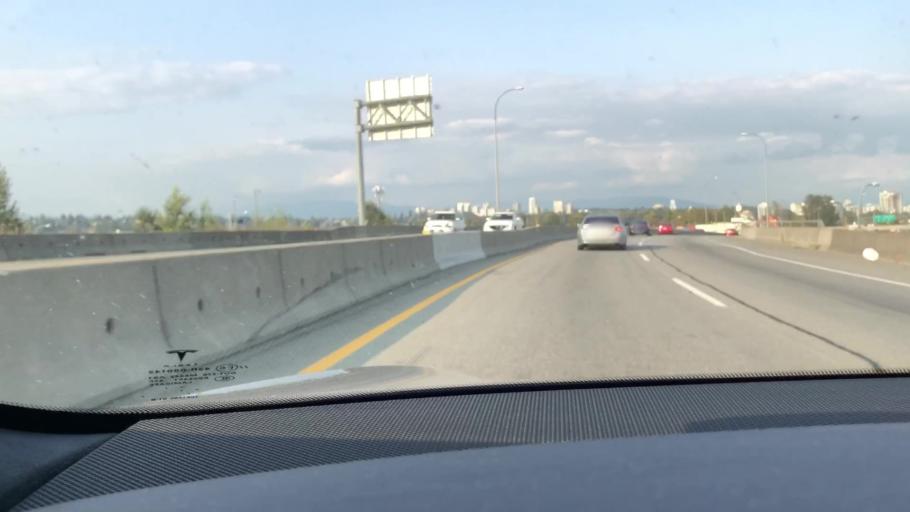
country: CA
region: British Columbia
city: New Westminster
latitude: 49.1874
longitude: -122.9520
